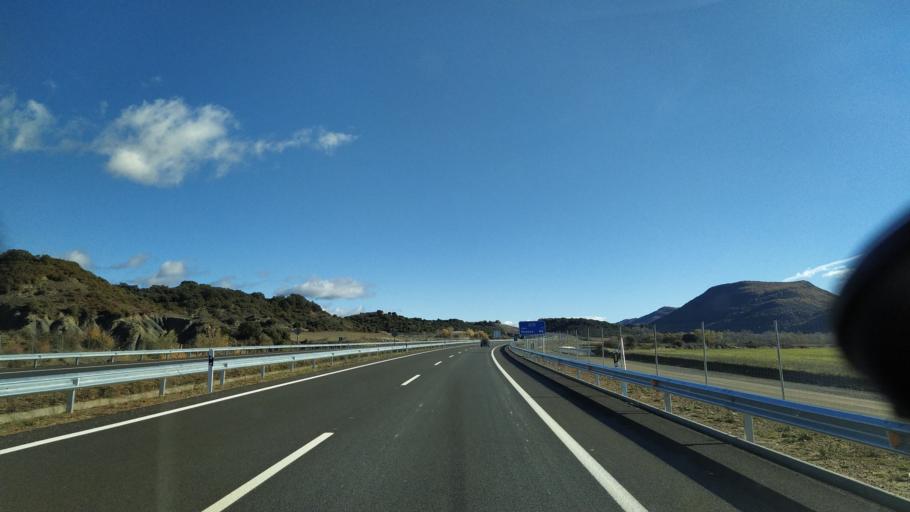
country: ES
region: Aragon
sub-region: Provincia de Huesca
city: Santa Cruz de la Seros
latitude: 42.5648
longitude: -0.7018
